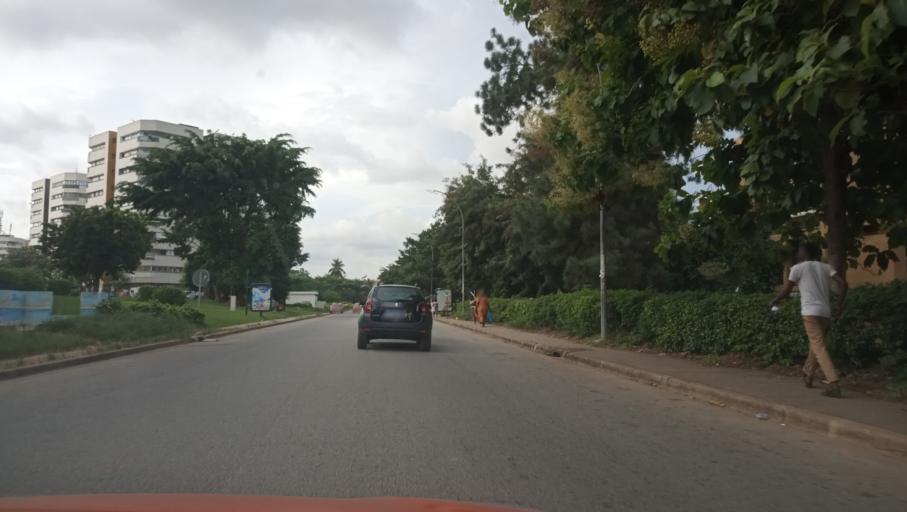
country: CI
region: Lagunes
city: Abidjan
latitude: 5.3411
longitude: -3.9763
